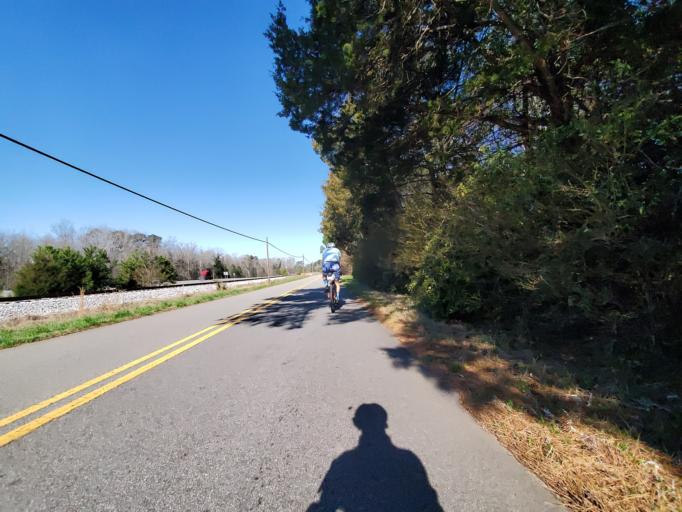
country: US
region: Georgia
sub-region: Clarke County
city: Country Club Estates
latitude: 33.9947
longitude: -83.4379
